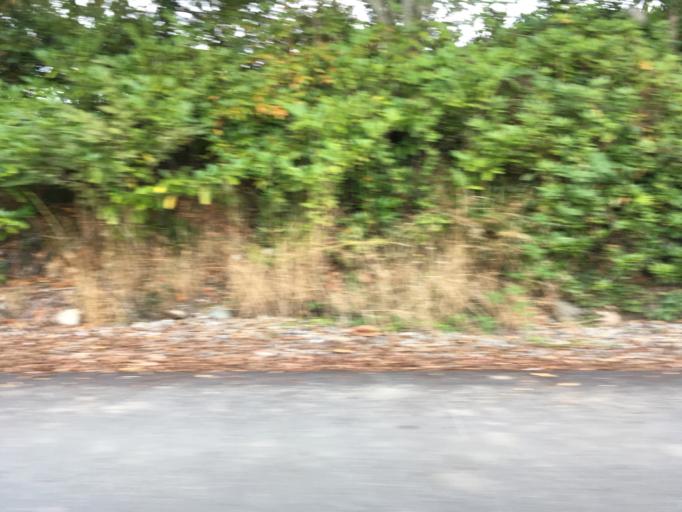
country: IE
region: Leinster
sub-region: Wicklow
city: Arklow
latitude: 52.8419
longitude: -6.1207
